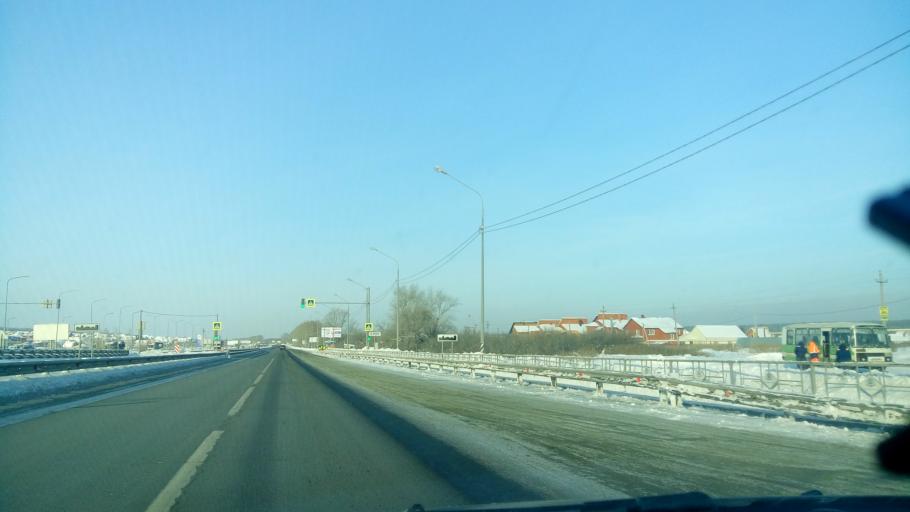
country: RU
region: Chelyabinsk
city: Dolgoderevenskoye
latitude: 55.2737
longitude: 61.3440
